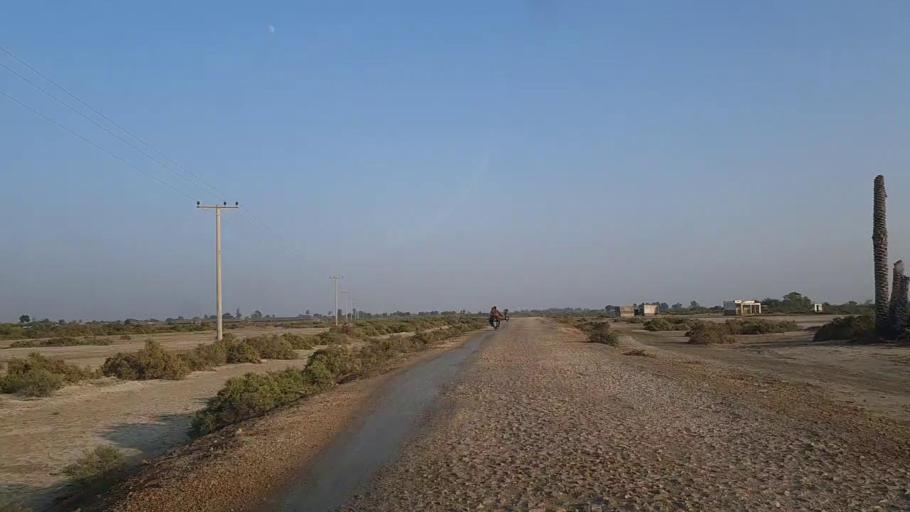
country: PK
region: Sindh
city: Keti Bandar
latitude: 24.2788
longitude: 67.6428
